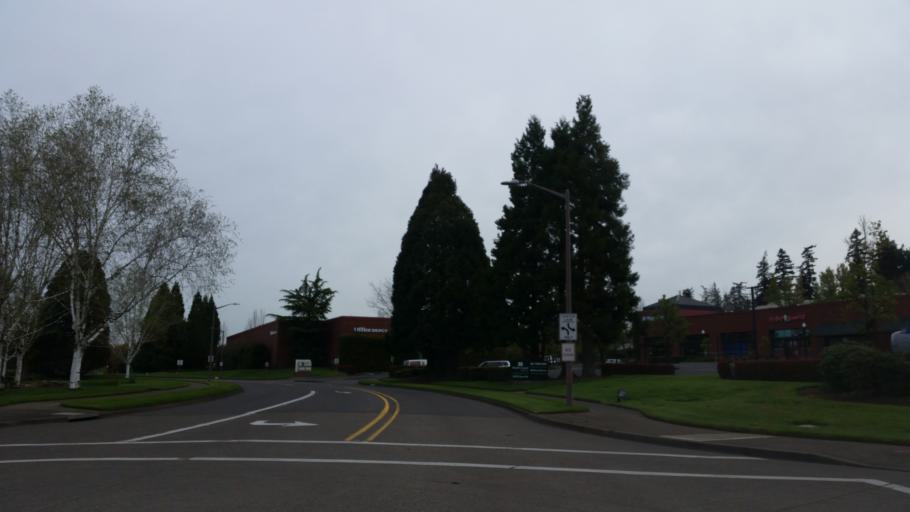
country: US
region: Oregon
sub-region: Washington County
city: Durham
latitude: 45.4097
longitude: -122.7468
